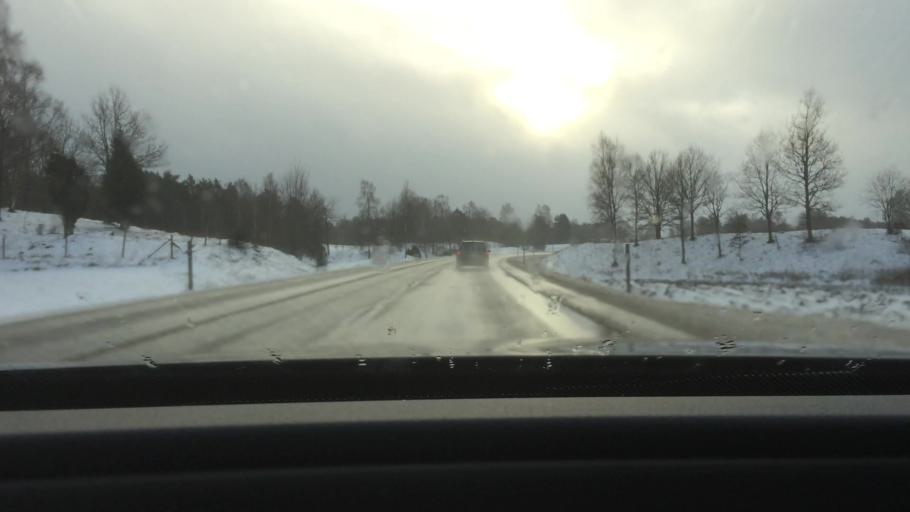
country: SE
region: Vaestra Goetaland
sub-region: Falkopings Kommun
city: Falkoeping
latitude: 57.9715
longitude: 13.5301
